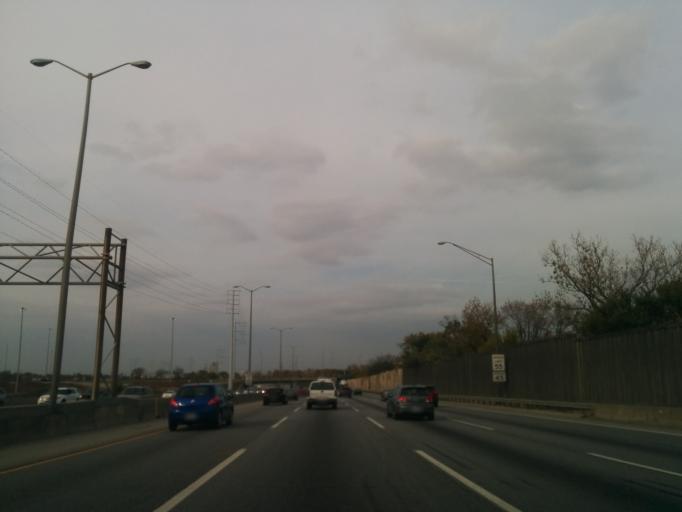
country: US
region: Illinois
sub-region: Cook County
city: Berkeley
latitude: 41.8868
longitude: -87.9186
